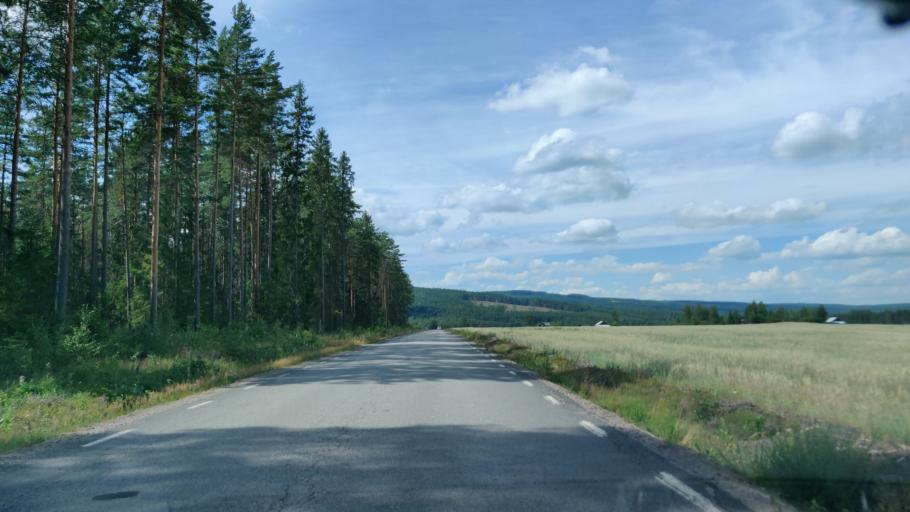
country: SE
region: Vaermland
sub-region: Hagfors Kommun
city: Ekshaerad
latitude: 60.0716
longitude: 13.5008
